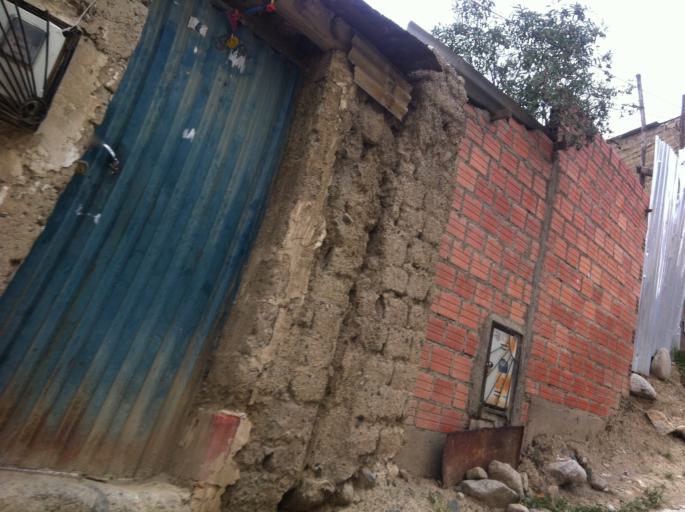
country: BO
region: La Paz
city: La Paz
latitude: -16.4741
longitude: -68.1235
